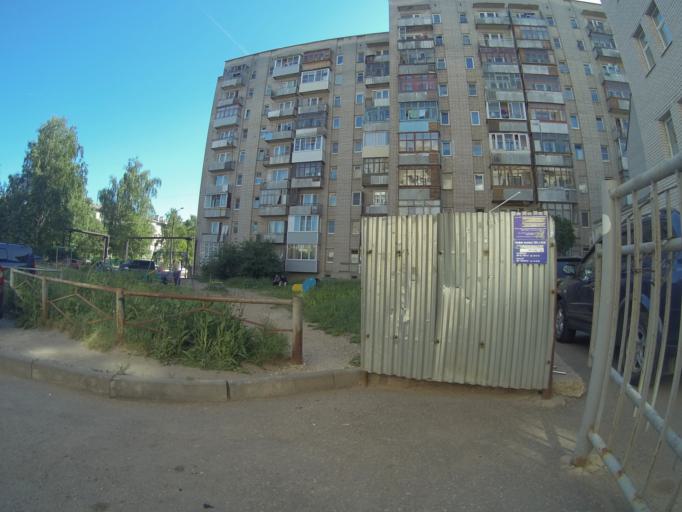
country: RU
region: Vladimir
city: Bogolyubovo
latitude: 56.1703
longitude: 40.4795
